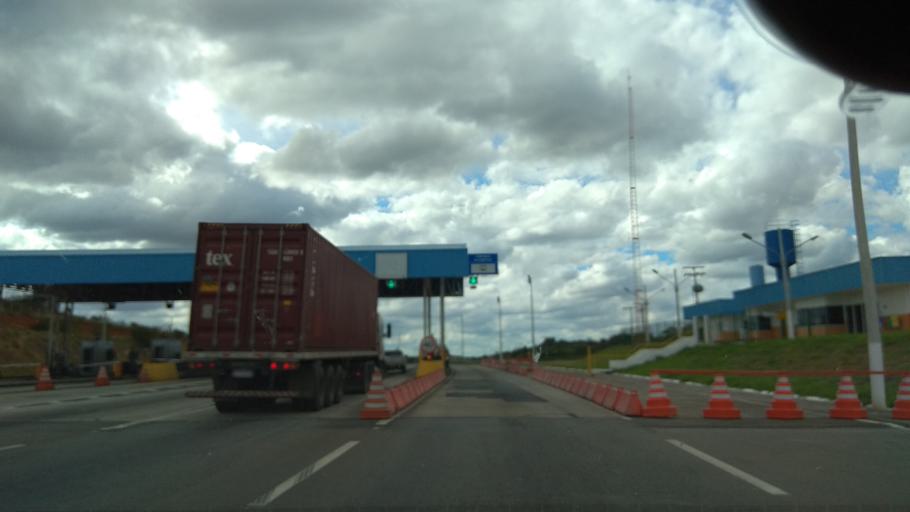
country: BR
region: Bahia
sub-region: Santa Ines
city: Santa Ines
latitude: -13.0093
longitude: -39.9570
